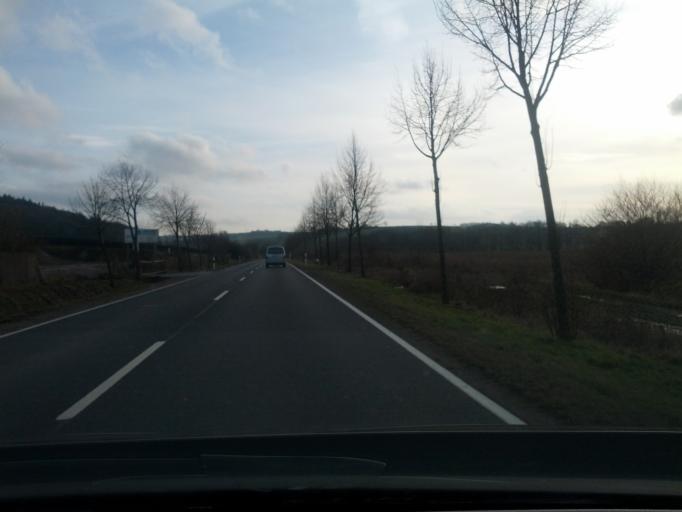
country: DE
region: Thuringia
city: Creuzburg
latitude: 51.0408
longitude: 10.2513
